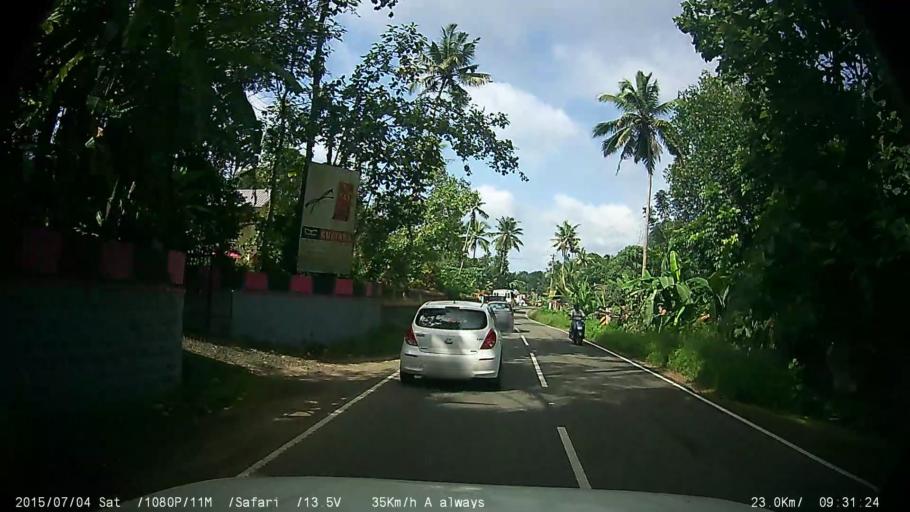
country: IN
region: Kerala
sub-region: Kottayam
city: Kottayam
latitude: 9.6289
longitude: 76.6051
